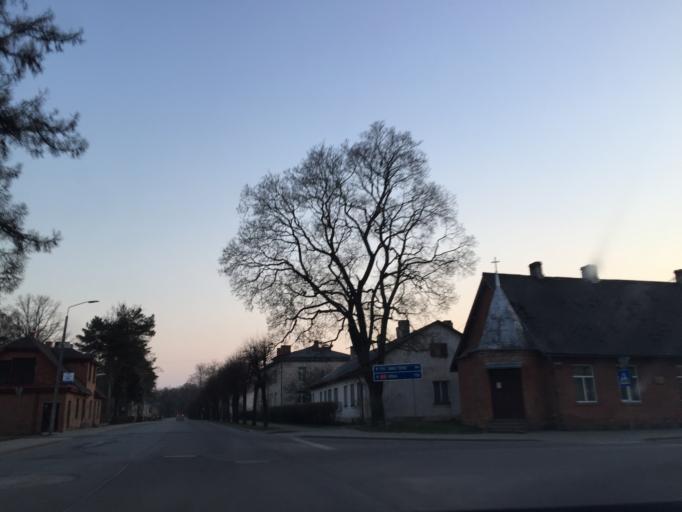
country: LV
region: Valkas Rajons
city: Valka
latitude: 57.7728
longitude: 26.0175
